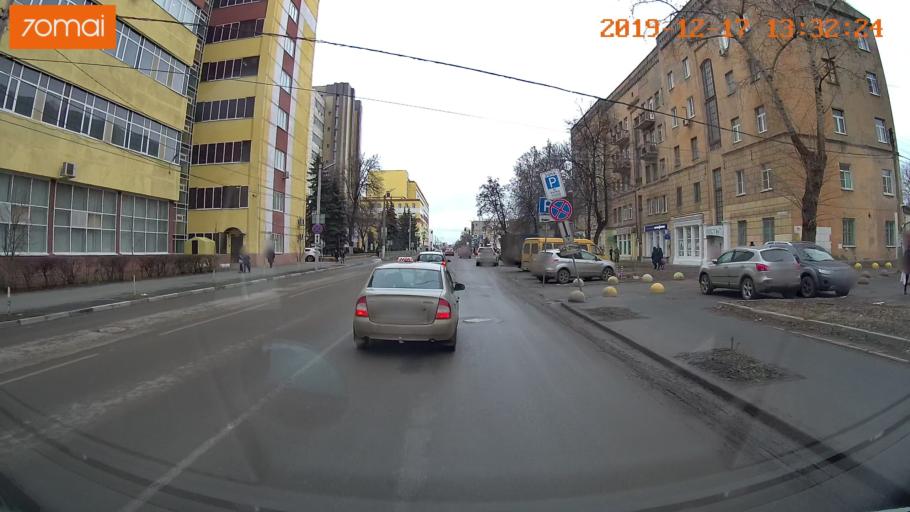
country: RU
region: Rjazan
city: Ryazan'
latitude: 54.6328
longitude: 39.7256
